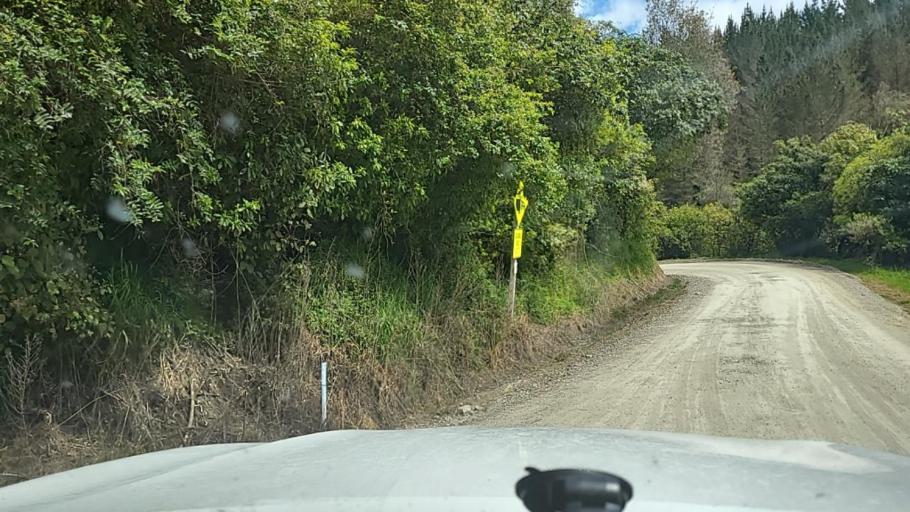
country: NZ
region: Gisborne
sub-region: Gisborne District
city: Gisborne
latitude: -38.8201
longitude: 177.7629
